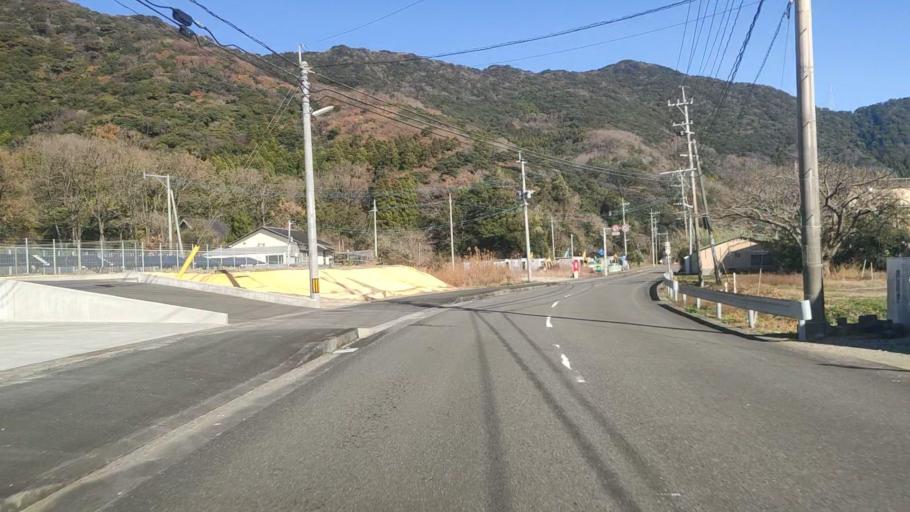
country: JP
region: Oita
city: Saiki
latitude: 32.8052
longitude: 131.9452
